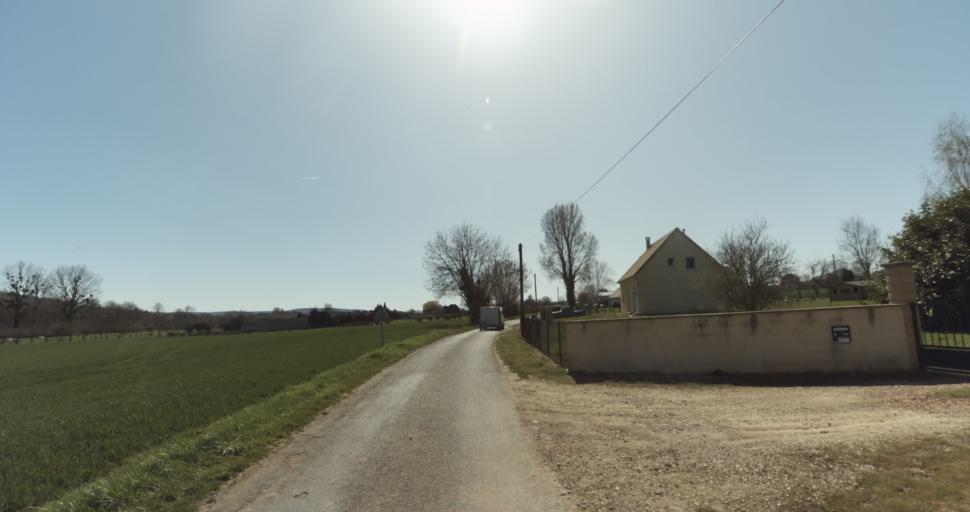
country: FR
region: Lower Normandy
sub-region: Departement du Calvados
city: Saint-Pierre-sur-Dives
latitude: 48.9924
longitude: 0.0282
